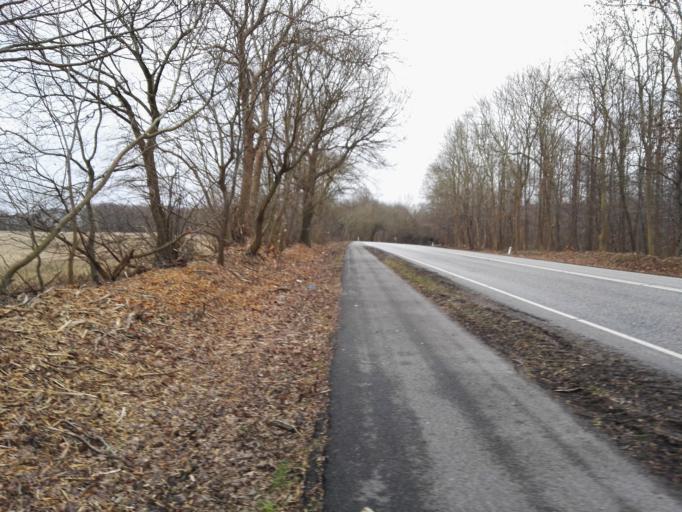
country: DK
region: Zealand
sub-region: Lejre Kommune
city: Norre Hvalso
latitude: 55.6473
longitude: 11.9122
